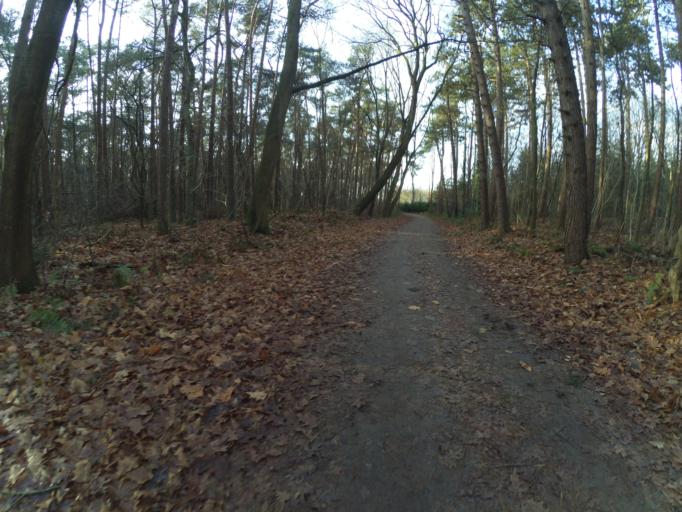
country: NL
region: North Brabant
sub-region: Gemeente Rucphen
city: Rucphen
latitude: 51.5232
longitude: 4.5465
